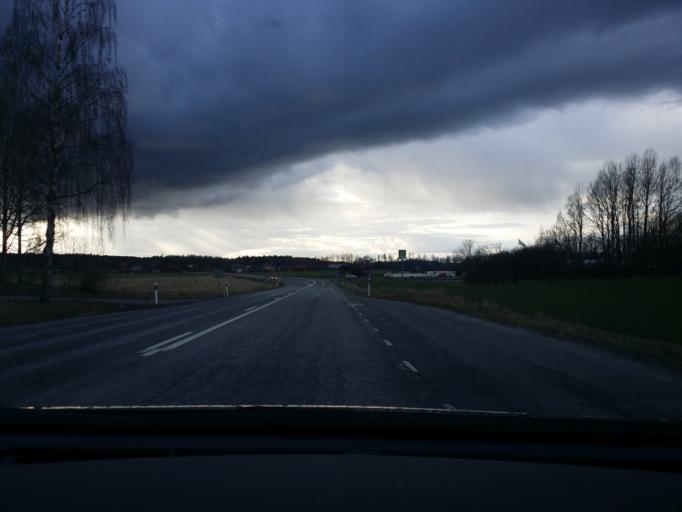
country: SE
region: Soedermanland
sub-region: Eskilstuna Kommun
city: Arla
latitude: 59.3875
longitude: 16.6501
